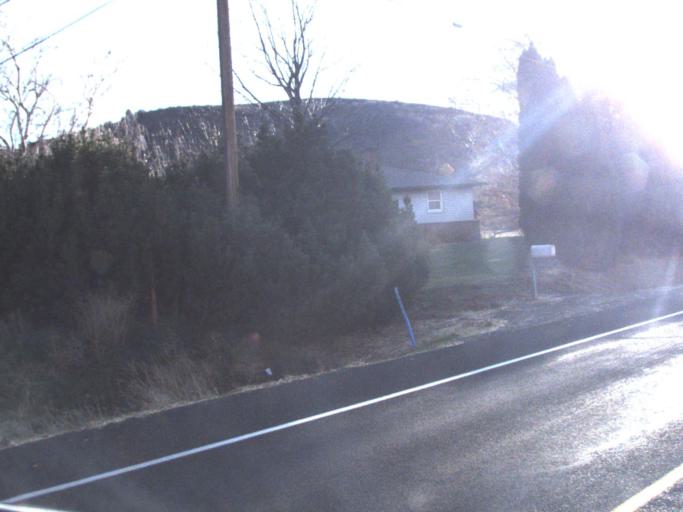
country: US
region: Washington
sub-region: Columbia County
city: Dayton
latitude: 46.2909
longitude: -118.0284
